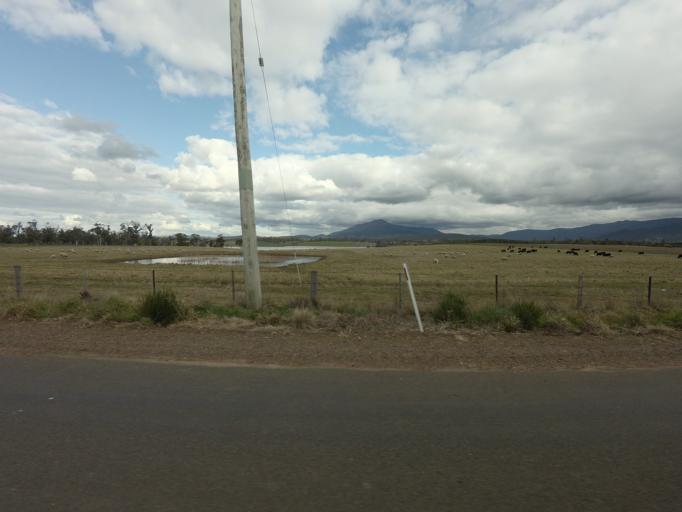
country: AU
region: Tasmania
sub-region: Northern Midlands
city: Longford
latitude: -41.8059
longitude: 147.1567
